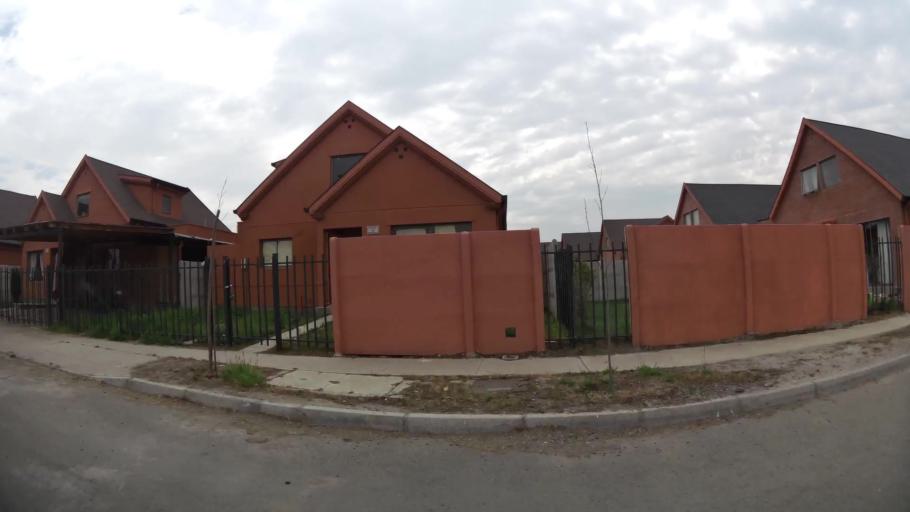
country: CL
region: Santiago Metropolitan
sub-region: Provincia de Chacabuco
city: Chicureo Abajo
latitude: -33.2159
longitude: -70.6667
